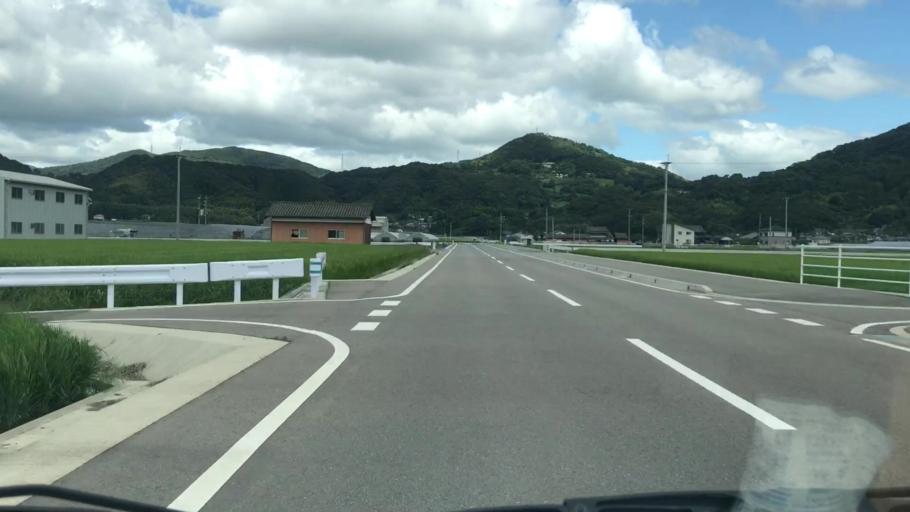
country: JP
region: Saga Prefecture
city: Kashima
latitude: 33.2214
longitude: 130.1455
